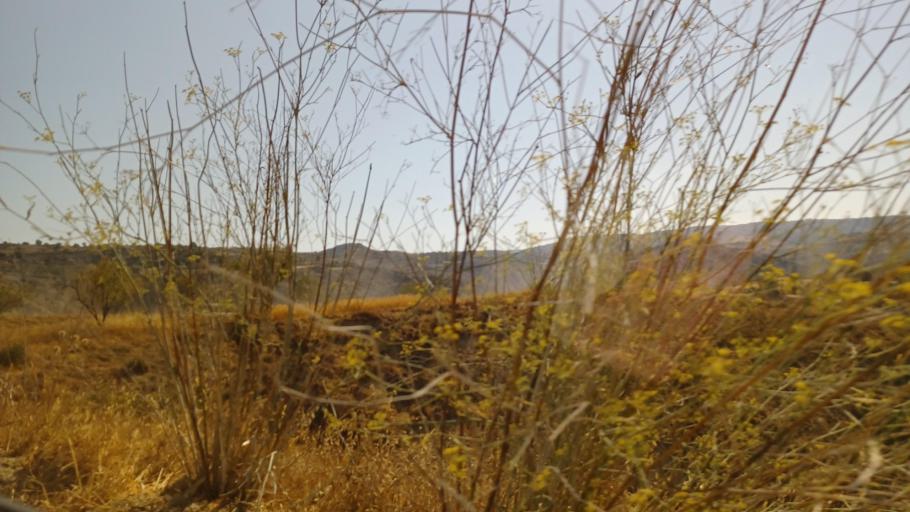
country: CY
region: Pafos
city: Pegeia
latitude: 34.9388
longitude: 32.4739
